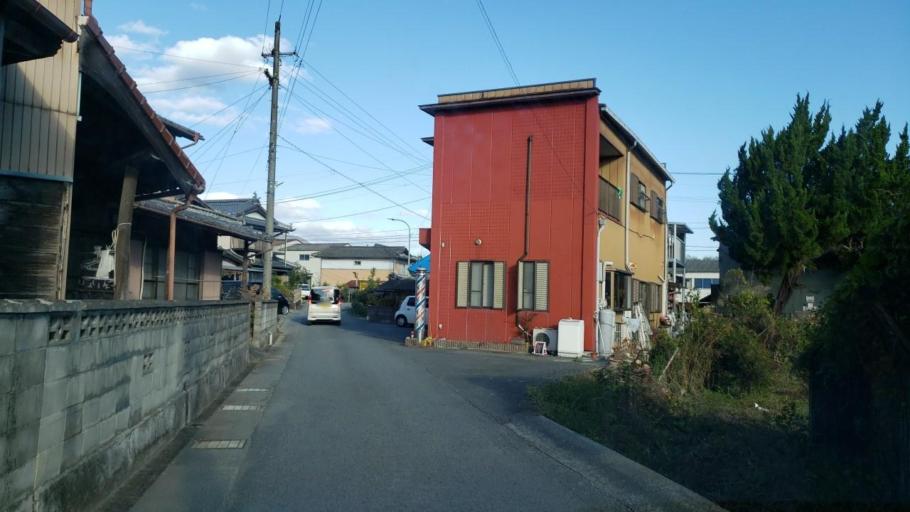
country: JP
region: Tokushima
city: Wakimachi
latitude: 34.0600
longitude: 134.0867
